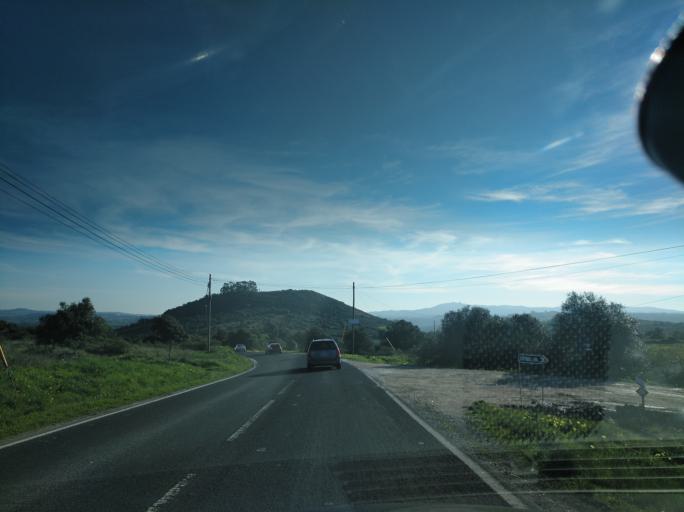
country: PT
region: Lisbon
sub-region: Mafra
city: Mafra
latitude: 38.9064
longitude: -9.3291
